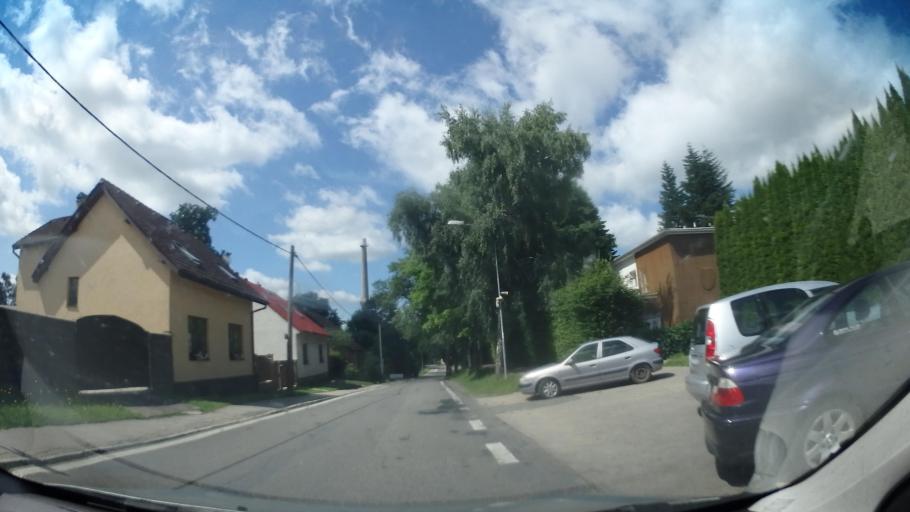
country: CZ
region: Vysocina
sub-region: Okres Zd'ar nad Sazavou
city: Zd'ar nad Sazavou
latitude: 49.5691
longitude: 15.9457
